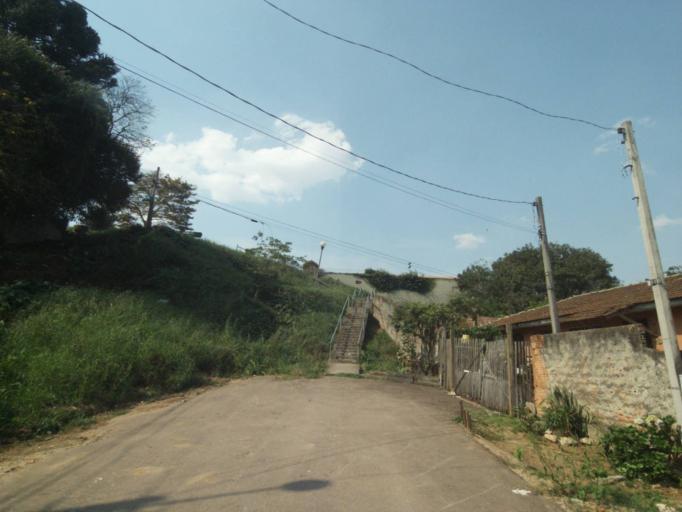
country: BR
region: Parana
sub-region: Curitiba
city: Curitiba
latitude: -25.4658
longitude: -49.2597
